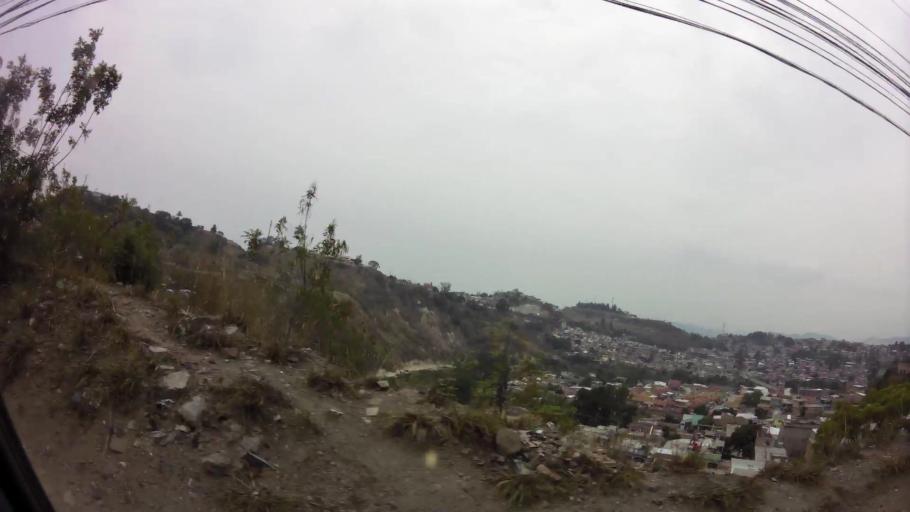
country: HN
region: Francisco Morazan
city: Tegucigalpa
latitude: 14.0805
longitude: -87.2256
